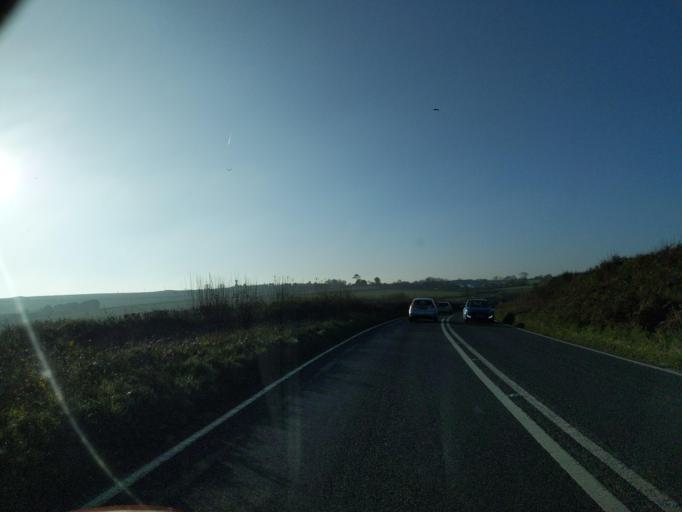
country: GB
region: England
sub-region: Cornwall
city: Liskeard
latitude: 50.4499
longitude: -4.5447
